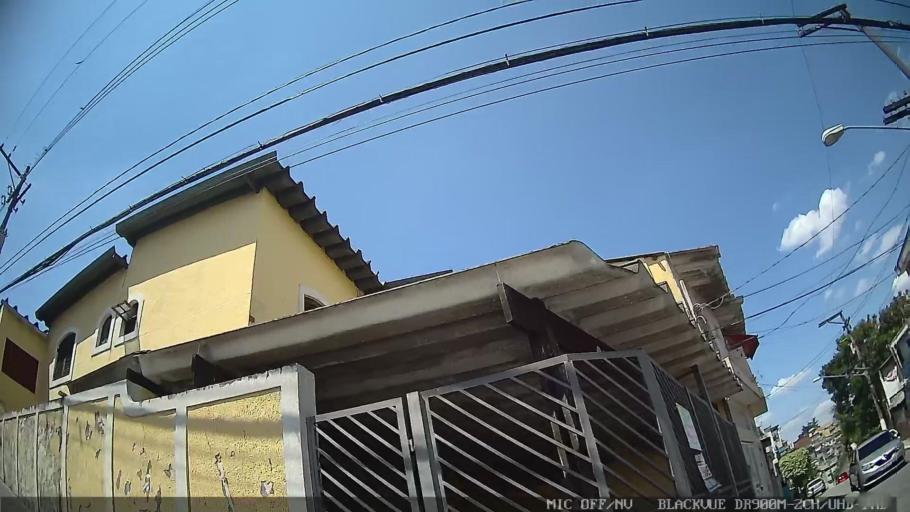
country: BR
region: Sao Paulo
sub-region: Guarulhos
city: Guarulhos
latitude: -23.5083
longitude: -46.5229
